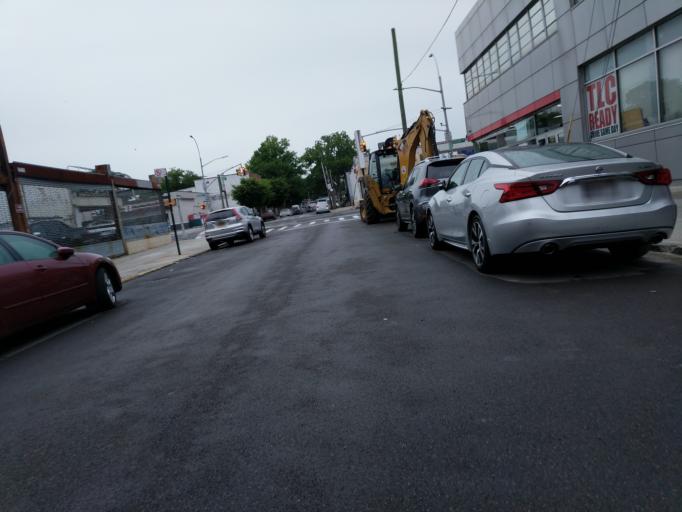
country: US
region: New York
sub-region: Queens County
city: Long Island City
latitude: 40.7536
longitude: -73.9002
